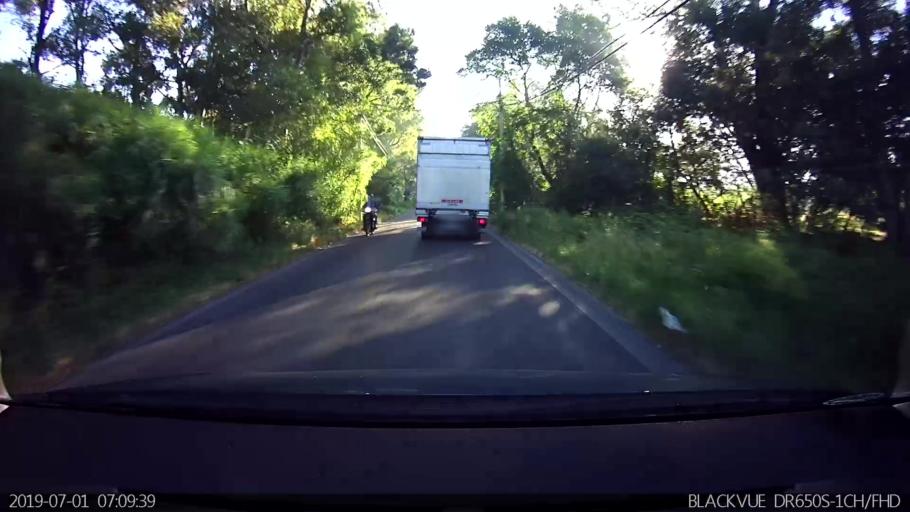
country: IT
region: Latium
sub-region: Provincia di Latina
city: Borgo Hermada
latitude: 41.3069
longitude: 13.1632
